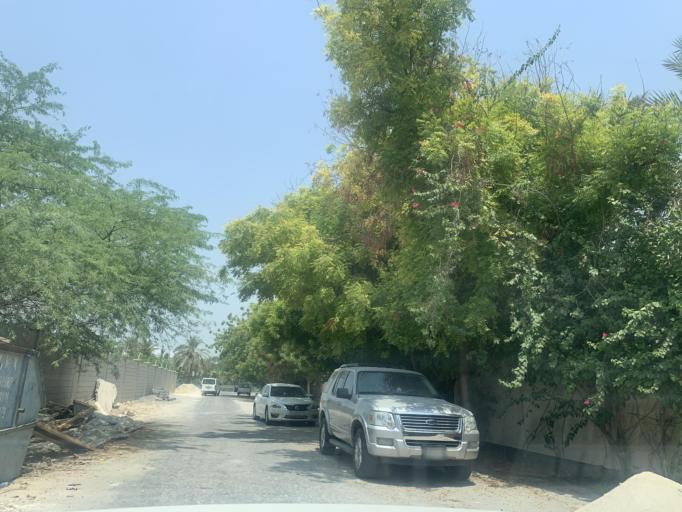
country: BH
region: Central Governorate
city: Madinat Hamad
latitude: 26.1488
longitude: 50.4644
